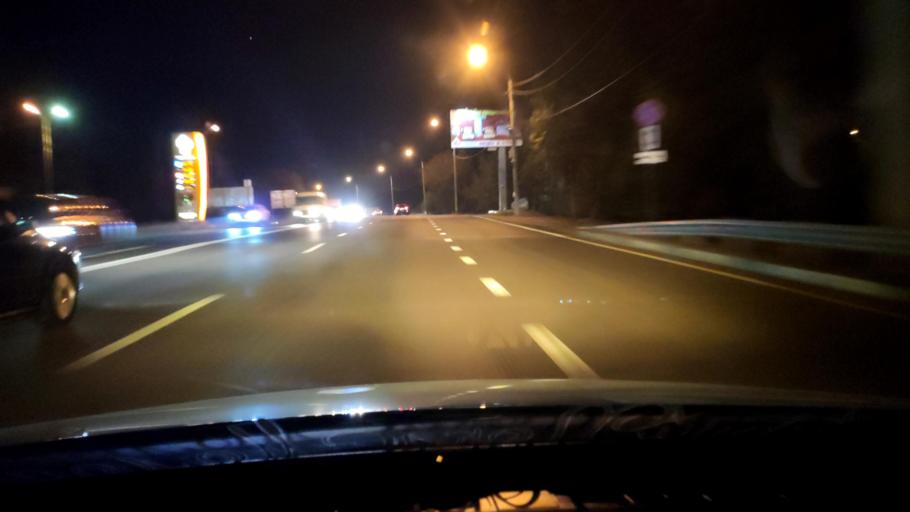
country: RU
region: Voronezj
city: Pridonskoy
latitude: 51.6808
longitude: 39.1161
